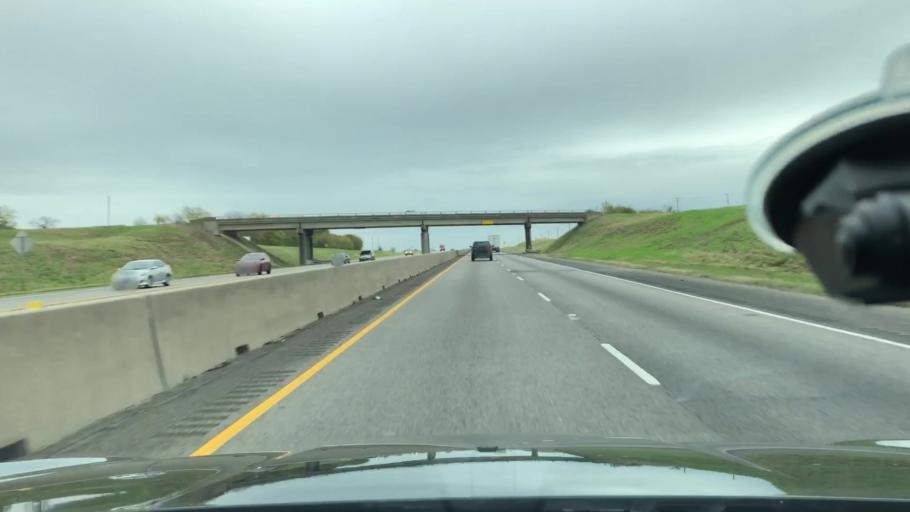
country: US
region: Texas
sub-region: Hopkins County
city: Sulphur Springs
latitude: 33.1467
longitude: -95.4959
